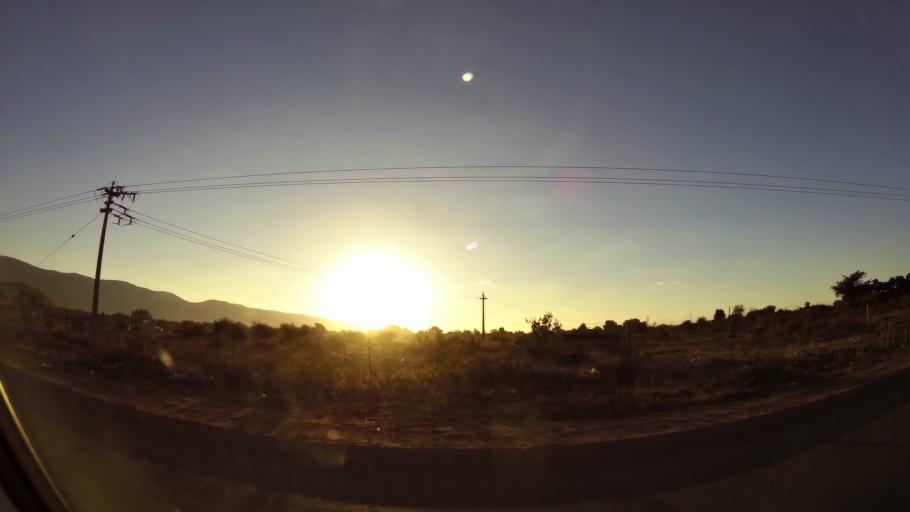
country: ZA
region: Limpopo
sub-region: Waterberg District Municipality
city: Mokopane
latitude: -24.1398
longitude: 28.9805
